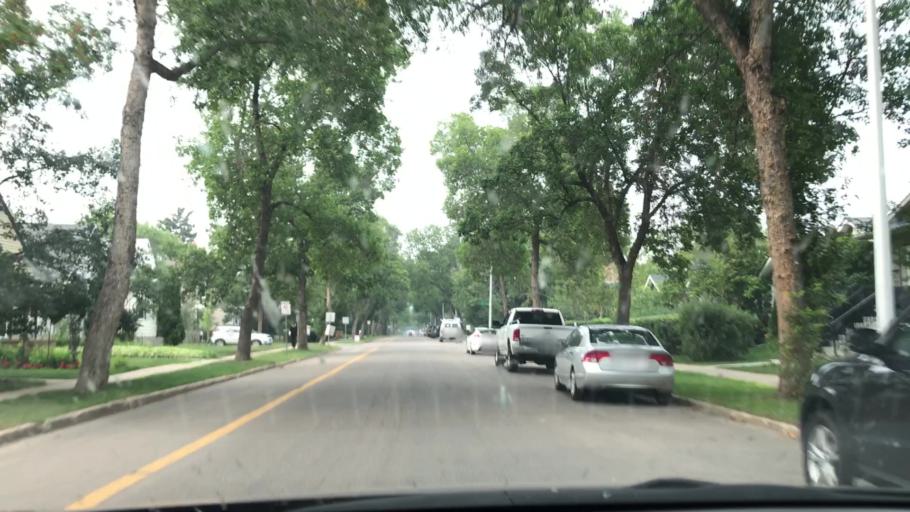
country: CA
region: Alberta
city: Edmonton
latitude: 53.5597
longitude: -113.5412
